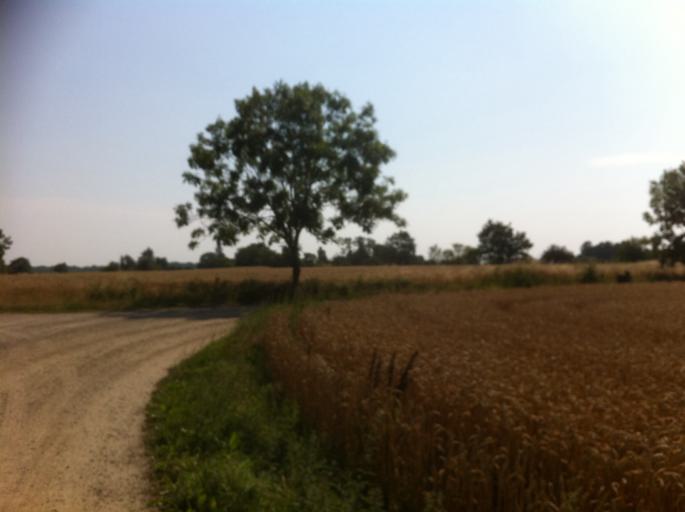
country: SE
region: Skane
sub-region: Lunds Kommun
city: Genarp
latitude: 55.6921
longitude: 13.3289
